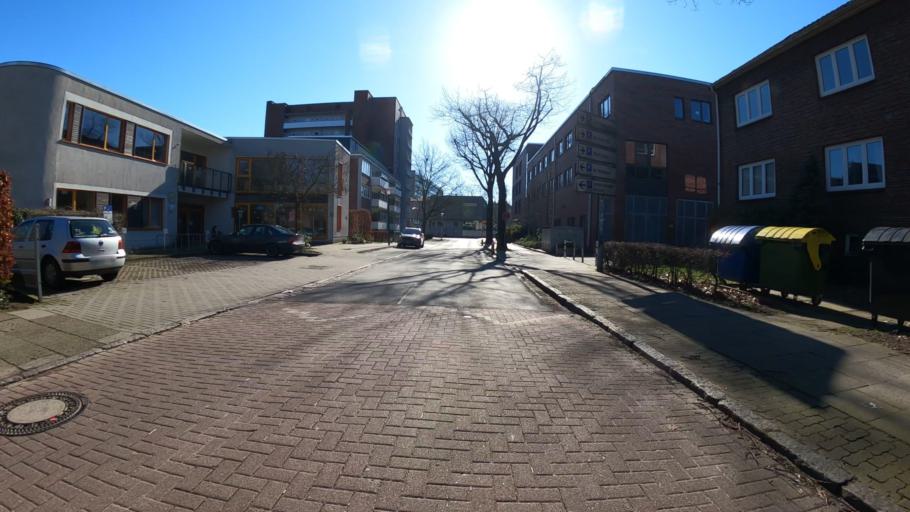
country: DE
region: Schleswig-Holstein
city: Pinneberg
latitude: 53.6637
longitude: 9.7966
